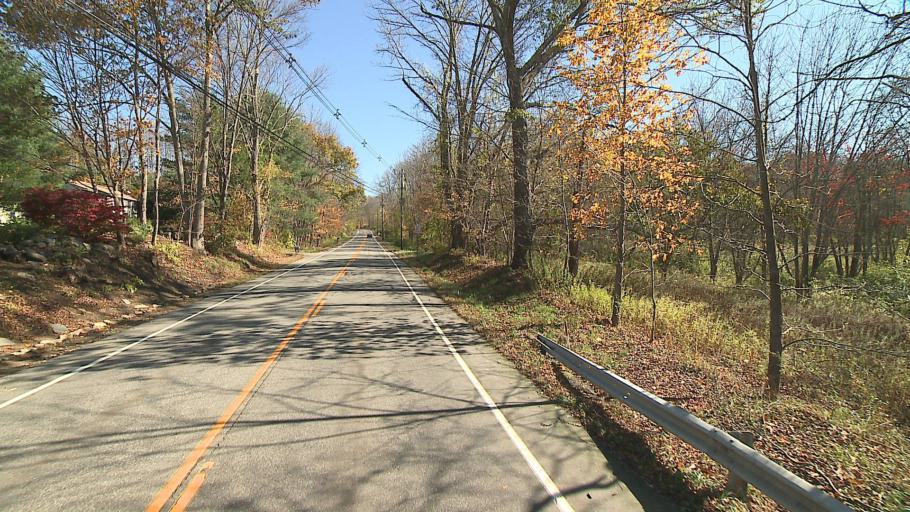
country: US
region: Connecticut
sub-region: Tolland County
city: Storrs
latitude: 41.8431
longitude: -72.2174
